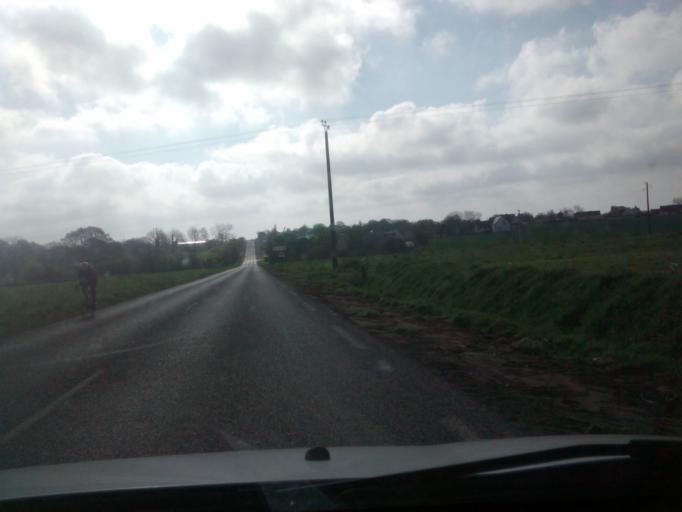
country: FR
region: Brittany
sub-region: Departement des Cotes-d'Armor
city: Trelevern
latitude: 48.7782
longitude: -3.3801
